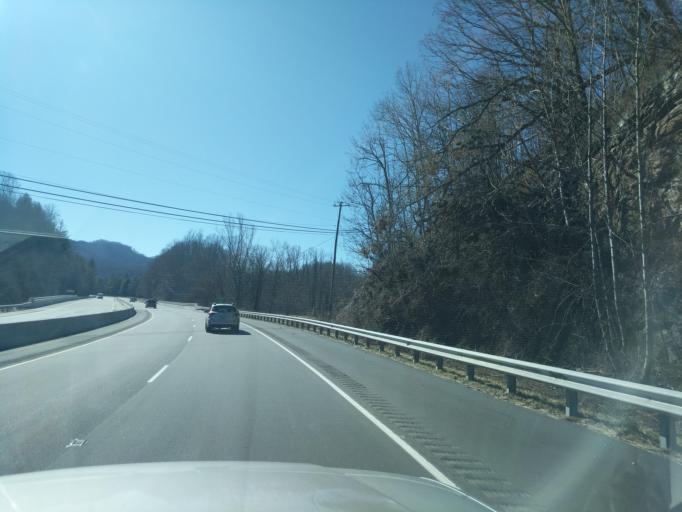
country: US
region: North Carolina
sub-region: Jackson County
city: Cullowhee
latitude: 35.4084
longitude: -83.1227
